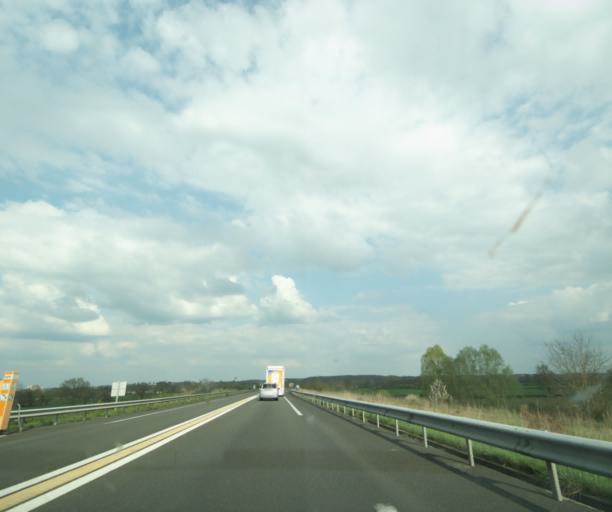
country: FR
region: Bourgogne
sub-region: Departement de Saone-et-Loire
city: Digoin
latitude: 46.4616
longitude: 3.9680
